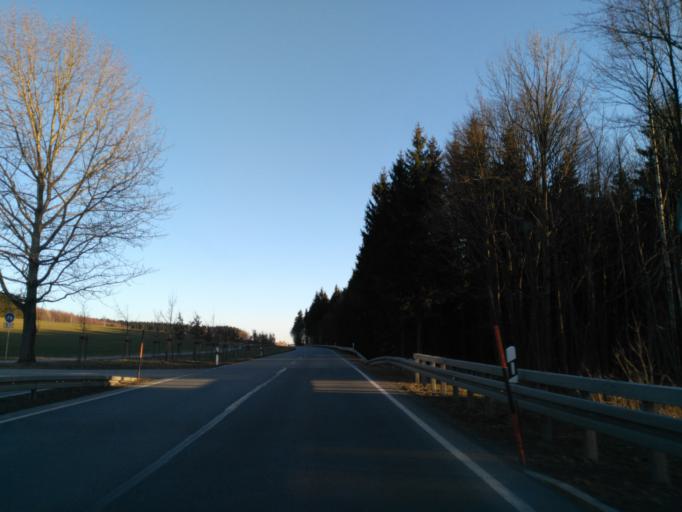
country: DE
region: Saxony
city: Konigswalde
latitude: 50.5368
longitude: 13.0238
